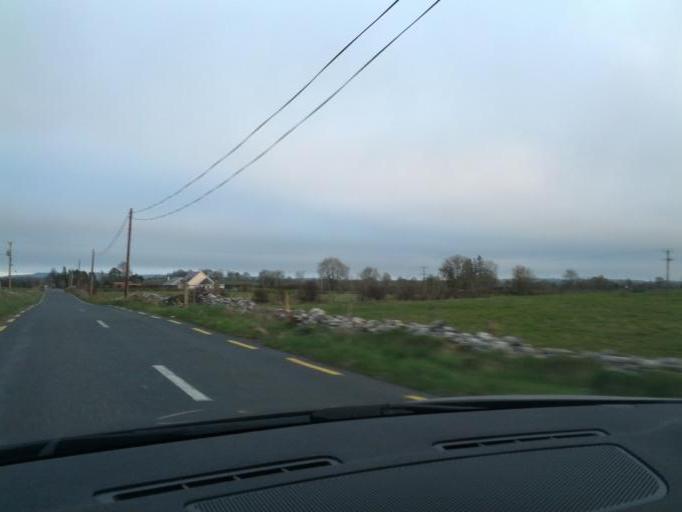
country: IE
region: Connaught
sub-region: Sligo
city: Ballymote
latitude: 54.0187
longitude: -8.5609
